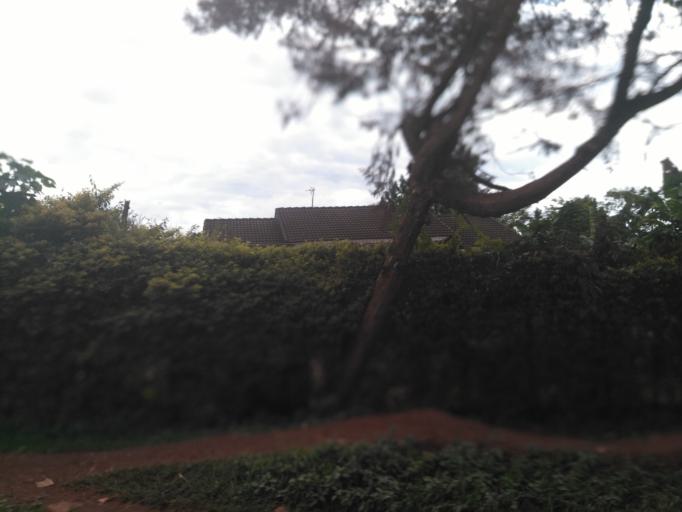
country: UG
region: Central Region
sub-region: Buikwe District
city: Njeru
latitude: 0.4093
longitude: 33.1805
